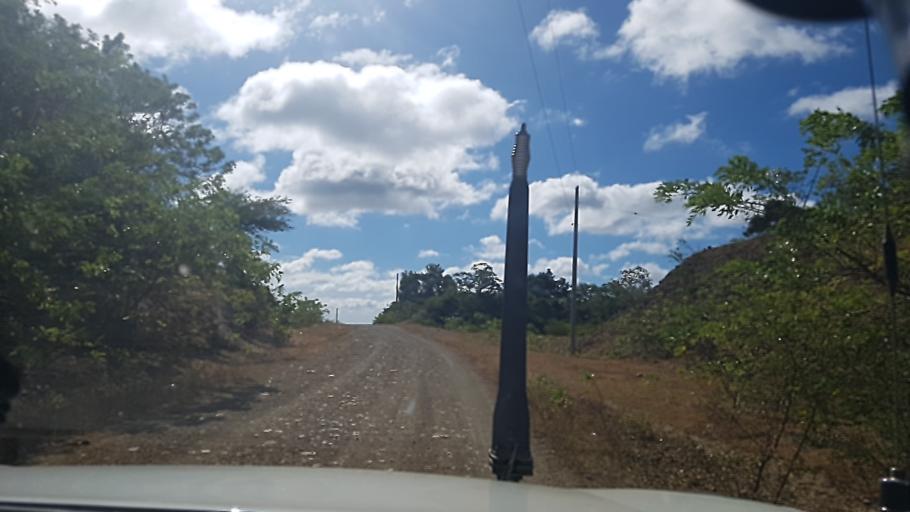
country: NI
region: Carazo
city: Santa Teresa
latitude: 11.6224
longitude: -86.1633
